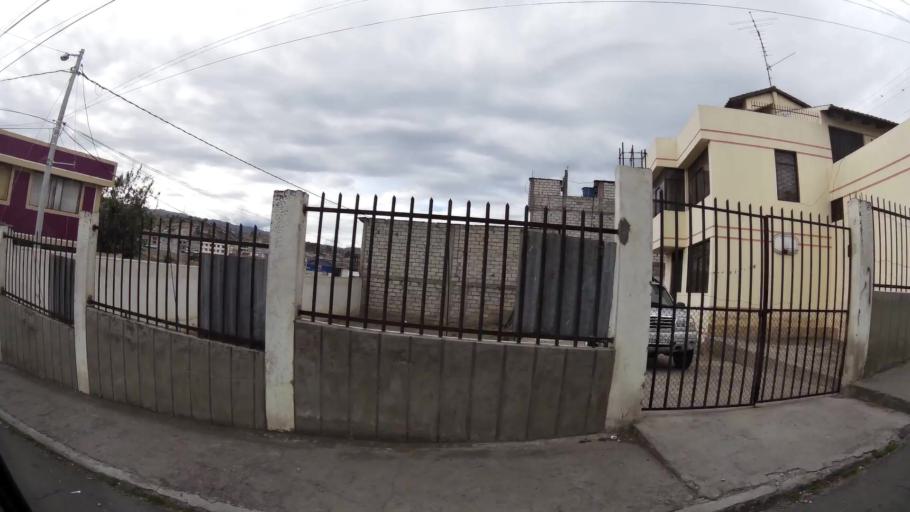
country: EC
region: Cotopaxi
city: Latacunga
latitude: -0.9276
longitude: -78.6271
